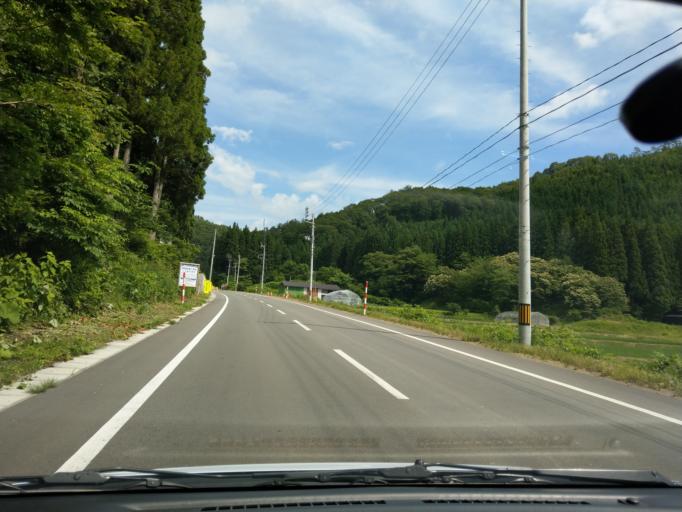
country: JP
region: Akita
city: Kakunodatemachi
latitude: 39.7192
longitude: 140.5854
